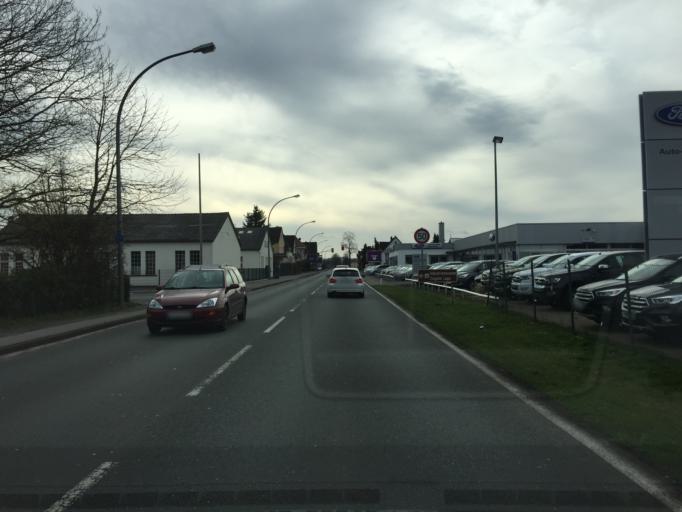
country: DE
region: North Rhine-Westphalia
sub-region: Regierungsbezirk Detmold
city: Lage
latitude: 52.0264
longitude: 8.7592
